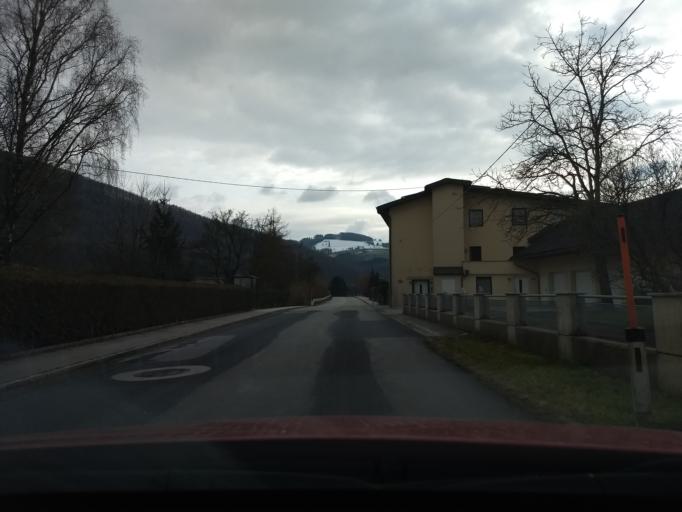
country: AT
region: Upper Austria
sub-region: Politischer Bezirk Steyr-Land
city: Garsten
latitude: 48.0079
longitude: 14.4065
